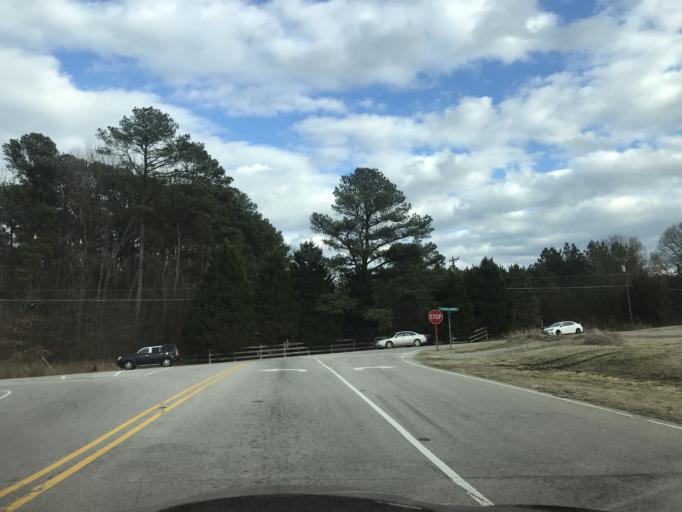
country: US
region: North Carolina
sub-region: Durham County
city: Durham
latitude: 35.9680
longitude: -78.8350
